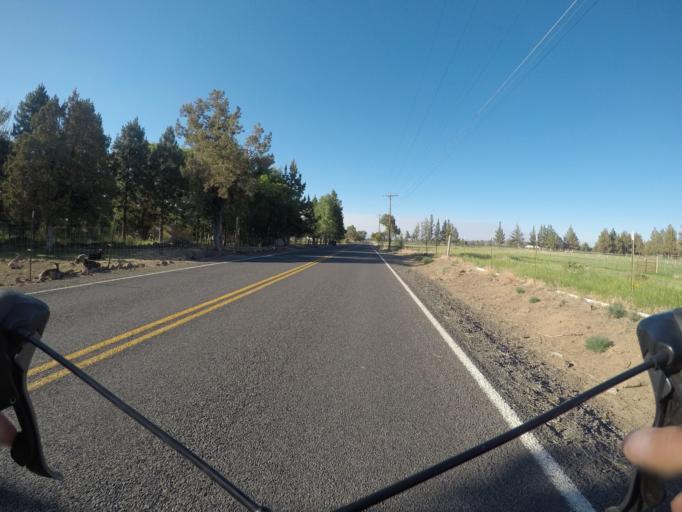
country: US
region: Oregon
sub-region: Deschutes County
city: Redmond
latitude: 44.2154
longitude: -121.2436
